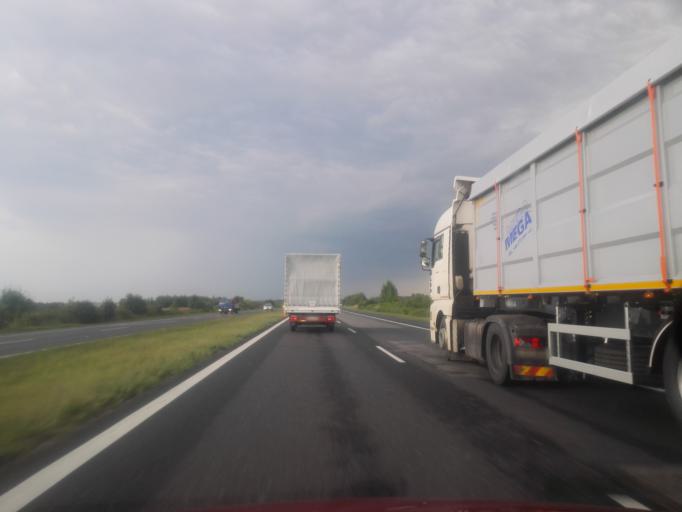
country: PL
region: Silesian Voivodeship
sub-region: Powiat czestochowski
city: Redziny
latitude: 50.8770
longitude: 19.1620
